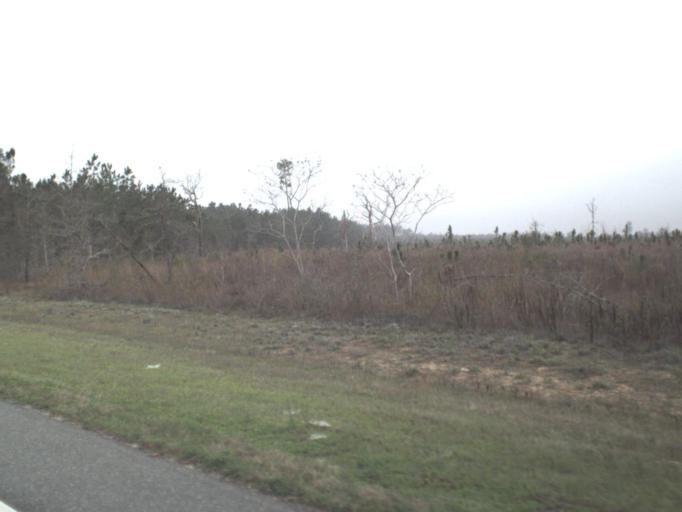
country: US
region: Florida
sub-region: Gadsden County
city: Gretna
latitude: 30.4544
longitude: -84.7498
